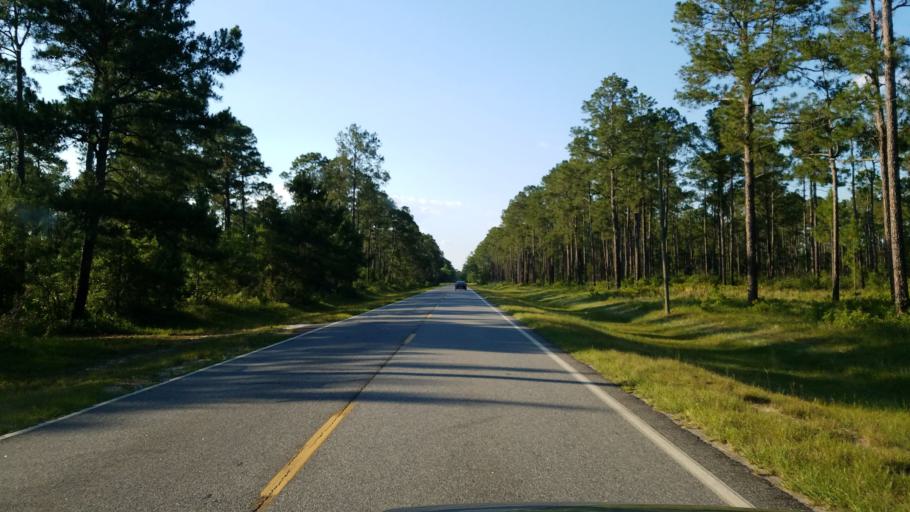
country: US
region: Georgia
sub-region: Lanier County
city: Lakeland
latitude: 30.9401
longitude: -83.0813
